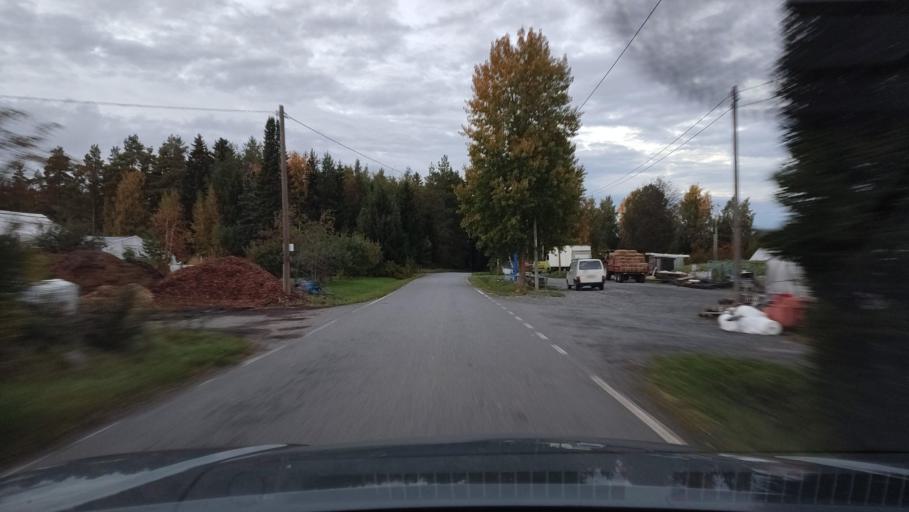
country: FI
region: Ostrobothnia
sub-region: Sydosterbotten
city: Kristinestad
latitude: 62.2723
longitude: 21.5105
